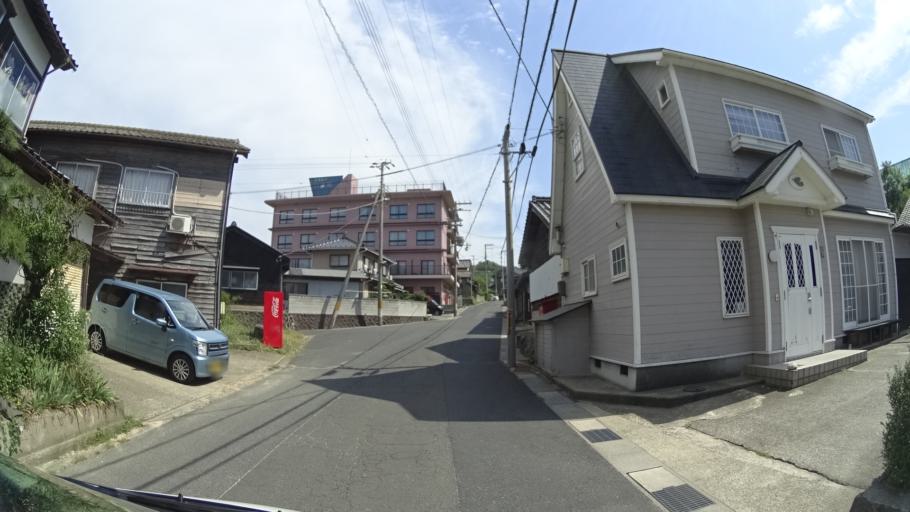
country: JP
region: Kyoto
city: Miyazu
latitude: 35.6986
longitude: 135.0547
